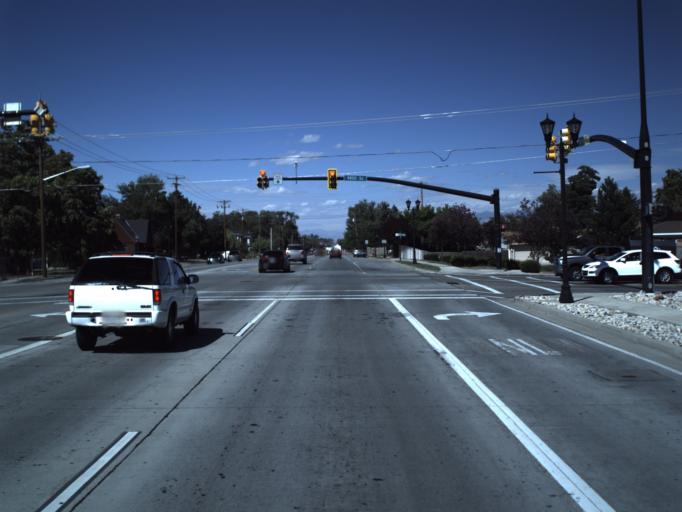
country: US
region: Utah
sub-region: Salt Lake County
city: South Jordan
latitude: 40.5727
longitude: -111.9386
